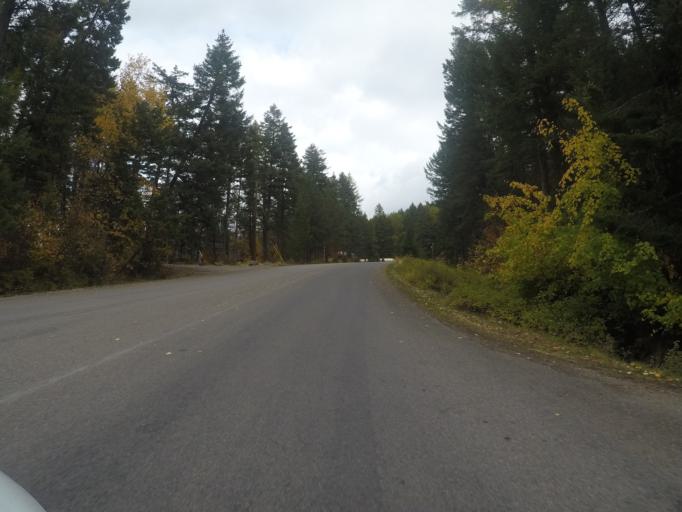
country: US
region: Montana
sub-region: Flathead County
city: Bigfork
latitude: 48.0549
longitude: -114.0751
